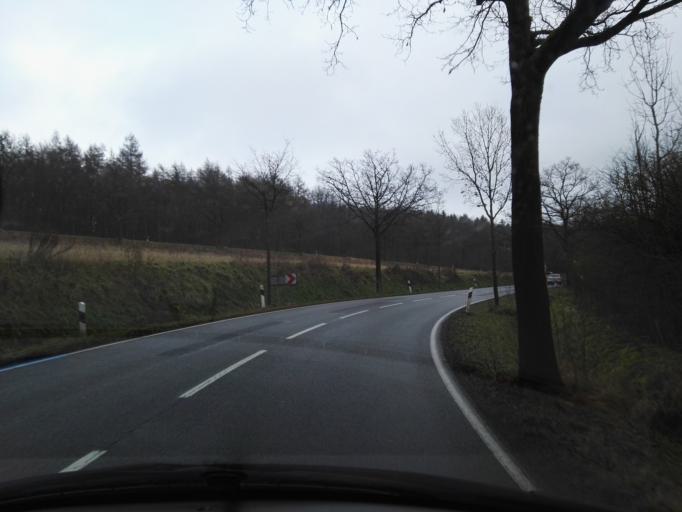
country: DE
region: Lower Saxony
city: Diekholzen
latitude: 52.0751
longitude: 9.9055
